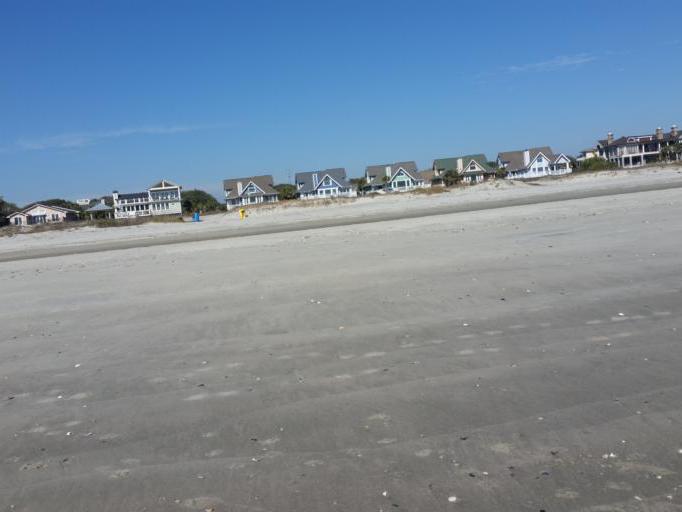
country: US
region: South Carolina
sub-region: Charleston County
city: Isle of Palms
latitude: 32.7961
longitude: -79.7569
